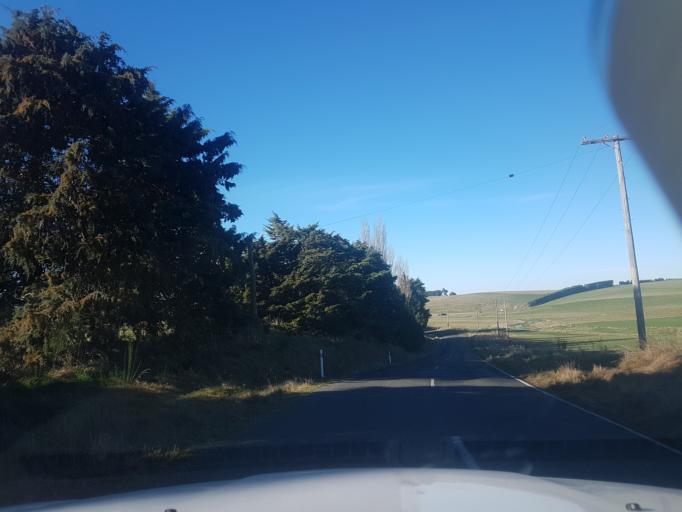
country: NZ
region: Canterbury
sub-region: Timaru District
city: Pleasant Point
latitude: -44.2758
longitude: 171.1162
